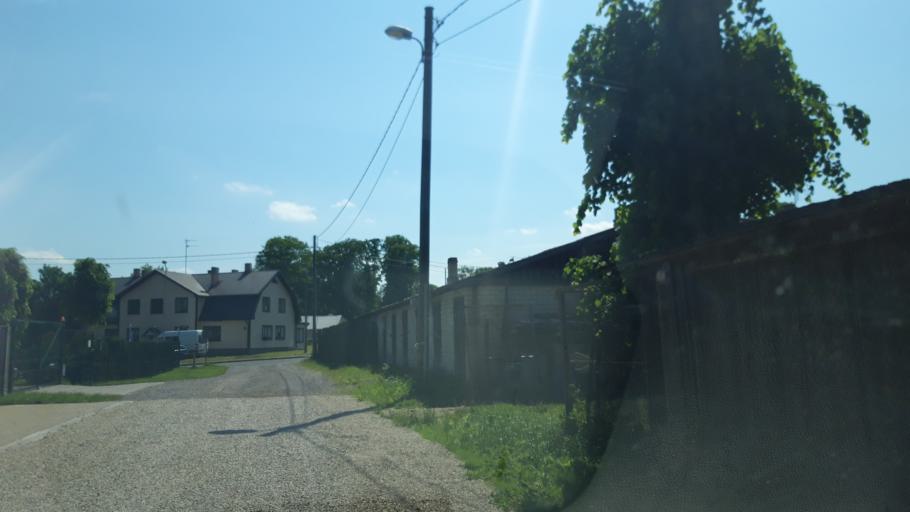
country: LV
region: Saulkrastu
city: Saulkrasti
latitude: 57.2595
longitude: 24.4123
